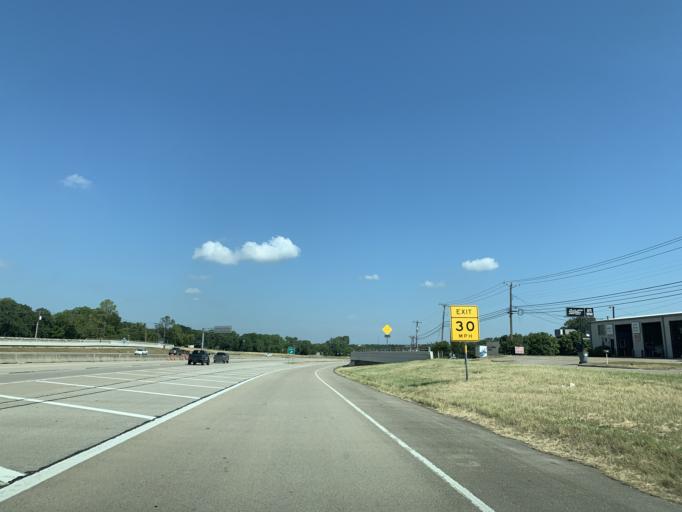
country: US
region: Texas
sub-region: Tarrant County
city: Azle
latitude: 32.8820
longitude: -97.5362
